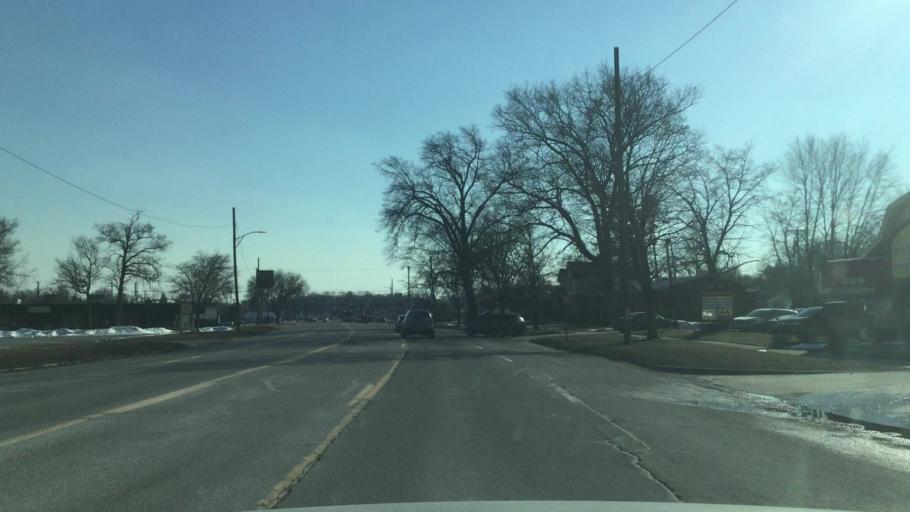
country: US
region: Michigan
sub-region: Wayne County
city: Westland
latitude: 42.3278
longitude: -83.3883
